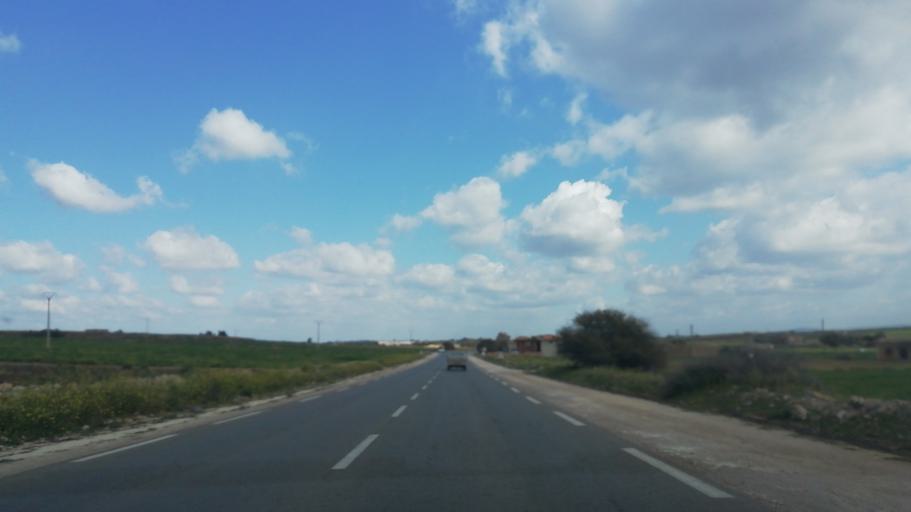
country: DZ
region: Relizane
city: Relizane
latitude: 35.7130
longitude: 0.2814
